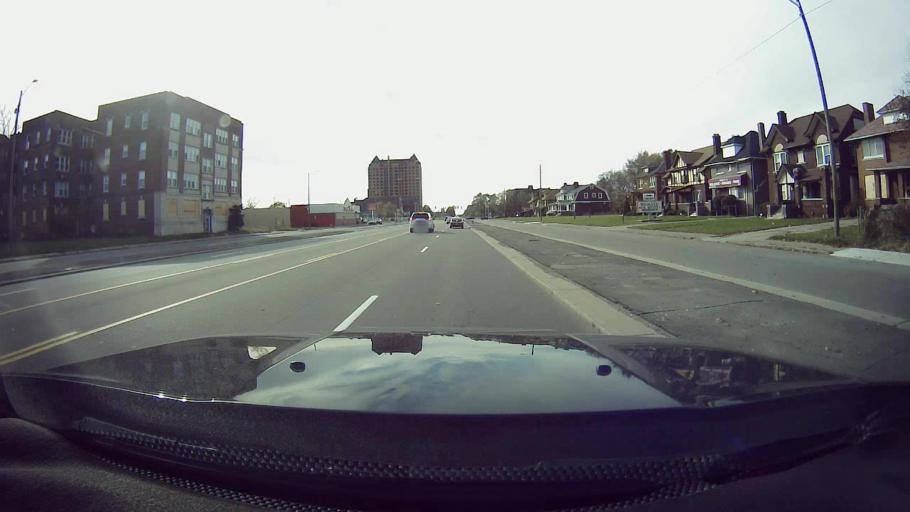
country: US
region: Michigan
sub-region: Wayne County
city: Highland Park
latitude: 42.3612
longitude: -83.0978
